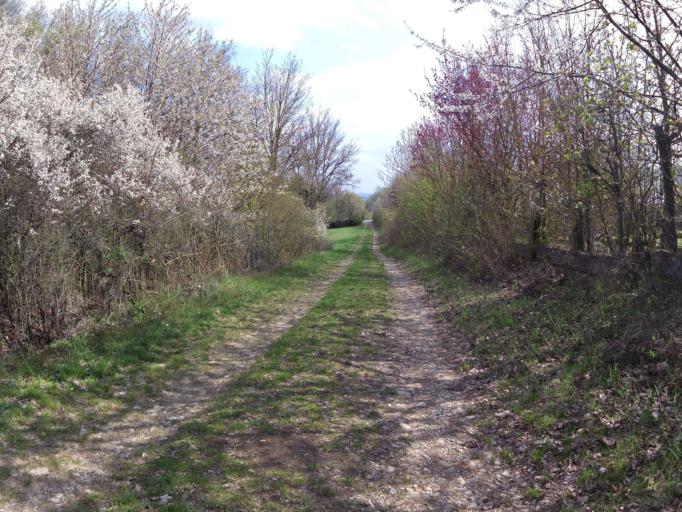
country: DE
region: Bavaria
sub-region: Regierungsbezirk Unterfranken
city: Rimpar
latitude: 49.8692
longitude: 9.9628
